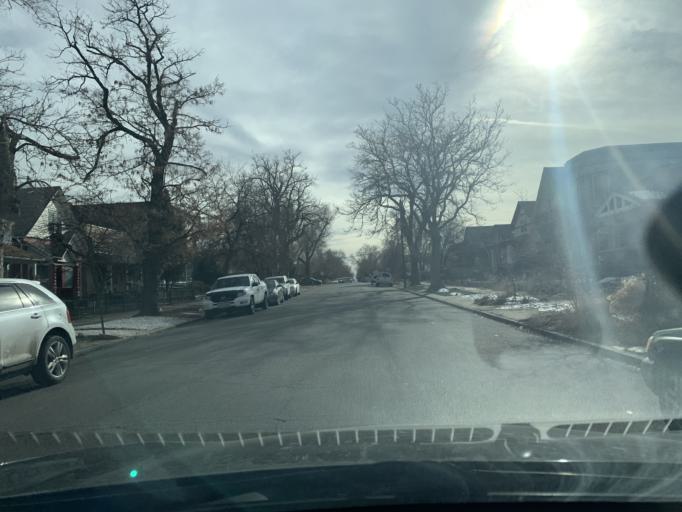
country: US
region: Colorado
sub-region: Denver County
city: Denver
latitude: 39.7378
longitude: -105.0016
